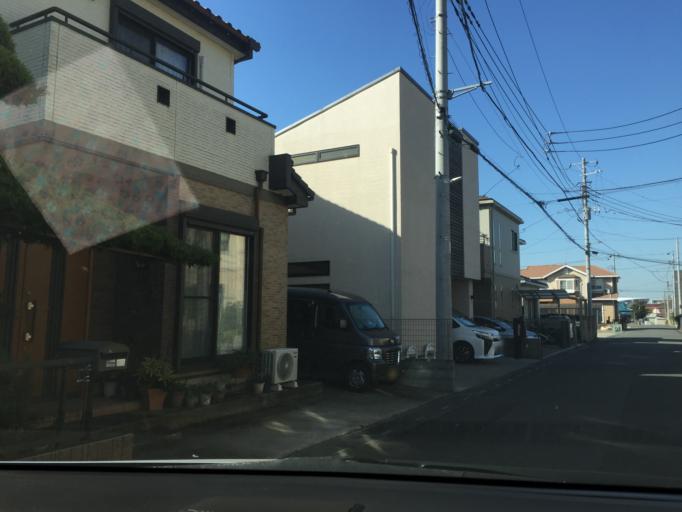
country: JP
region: Saitama
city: Koshigaya
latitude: 35.8898
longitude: 139.7291
